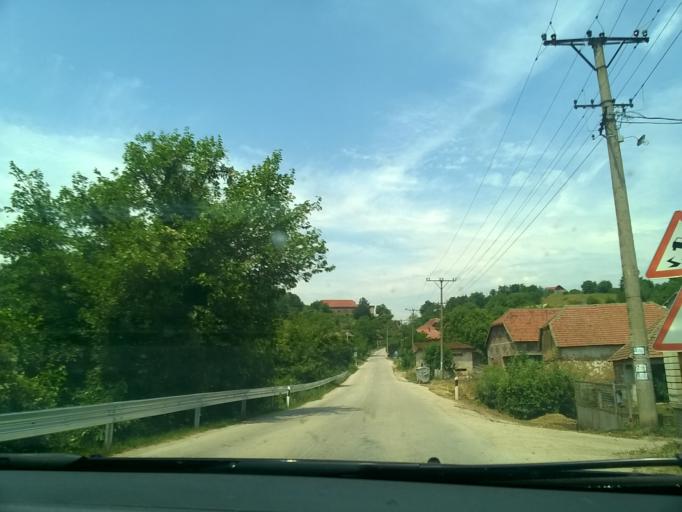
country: RS
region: Central Serbia
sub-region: Nisavski Okrug
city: Aleksinac
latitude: 43.6362
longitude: 21.7166
